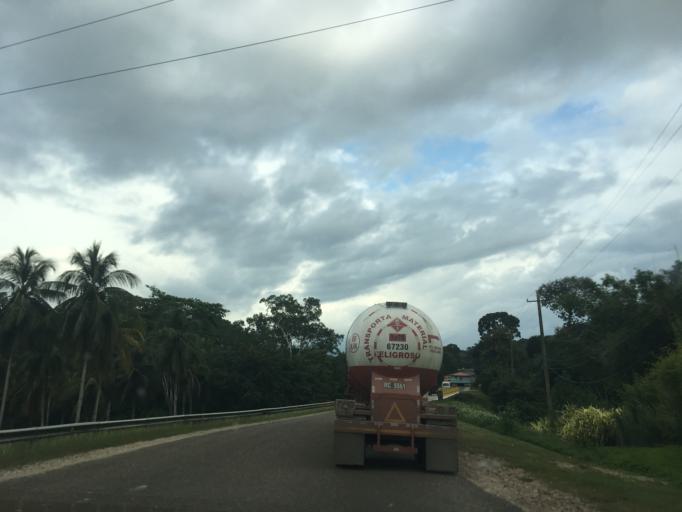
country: BZ
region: Cayo
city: San Ignacio
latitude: 17.2038
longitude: -88.9570
